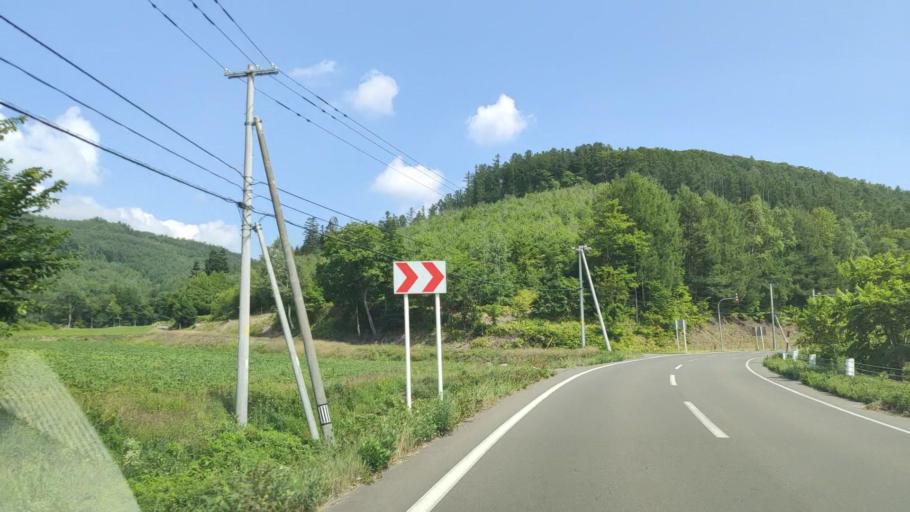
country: JP
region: Hokkaido
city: Shimo-furano
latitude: 43.4253
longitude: 142.3998
